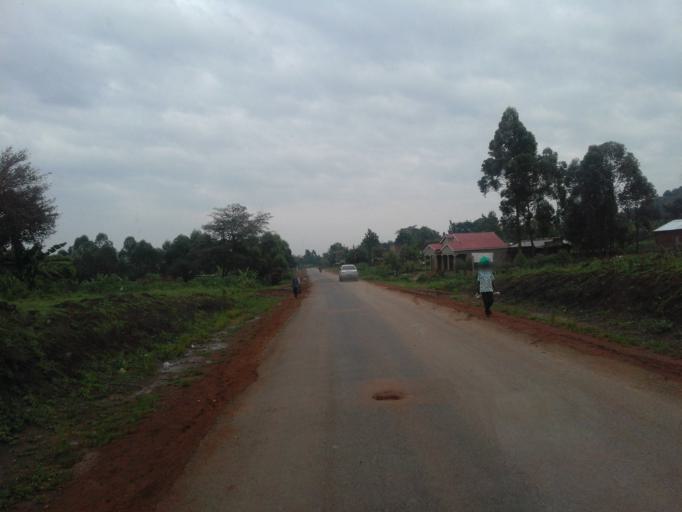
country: UG
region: Eastern Region
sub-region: Sironko District
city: Sironko
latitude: 1.1929
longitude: 34.1927
